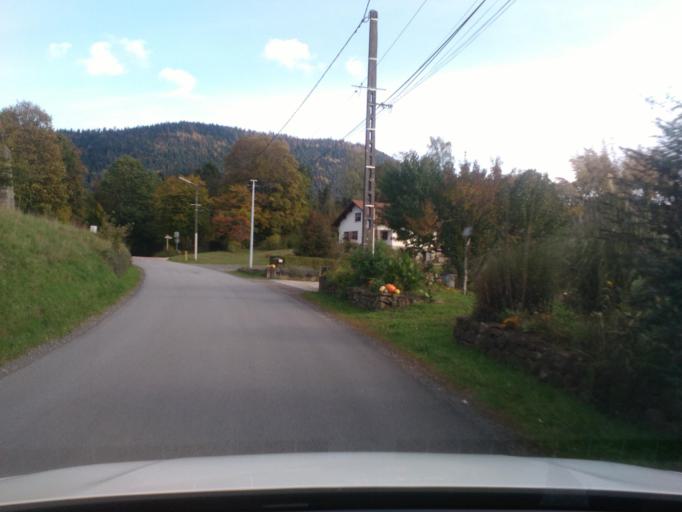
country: FR
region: Lorraine
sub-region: Departement des Vosges
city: Senones
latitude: 48.4148
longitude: 7.0454
